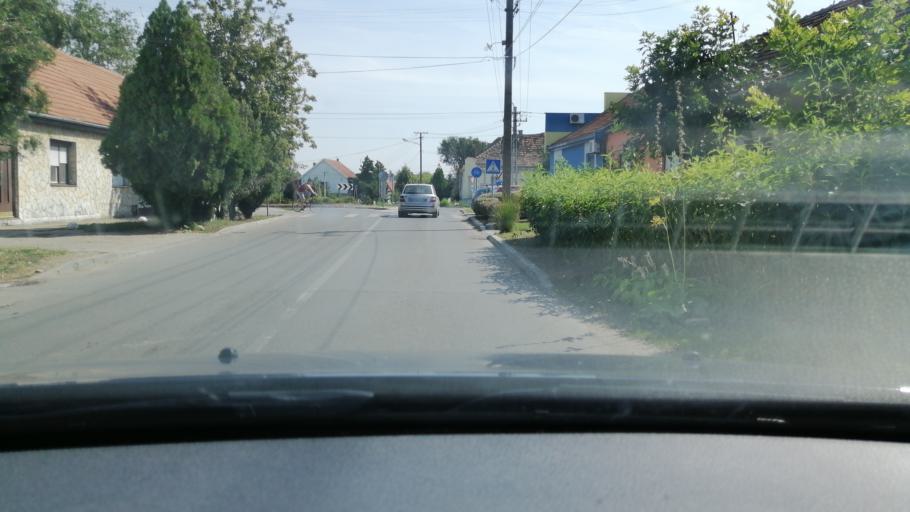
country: RS
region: Autonomna Pokrajina Vojvodina
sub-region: Srednjebanatski Okrug
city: Zrenjanin
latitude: 45.3878
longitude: 20.3796
